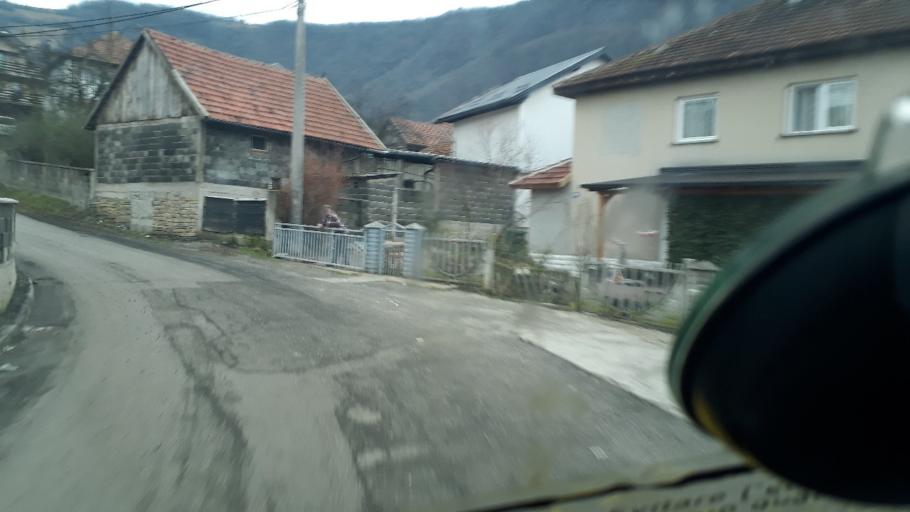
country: BA
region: Federation of Bosnia and Herzegovina
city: Zenica
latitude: 44.1521
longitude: 17.9724
